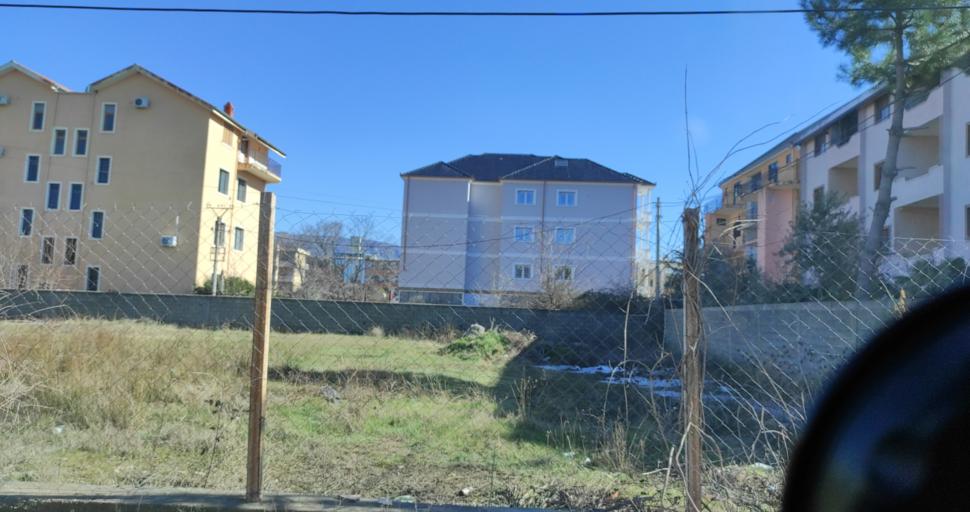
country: AL
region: Shkoder
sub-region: Rrethi i Shkodres
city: Velipoje
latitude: 41.8651
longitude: 19.4212
